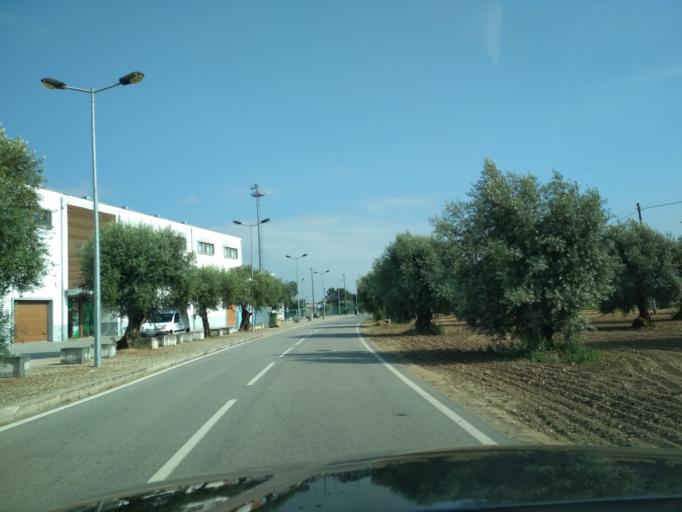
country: PT
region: Aveiro
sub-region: Mealhada
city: Mealhada
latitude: 40.3743
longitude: -8.4563
